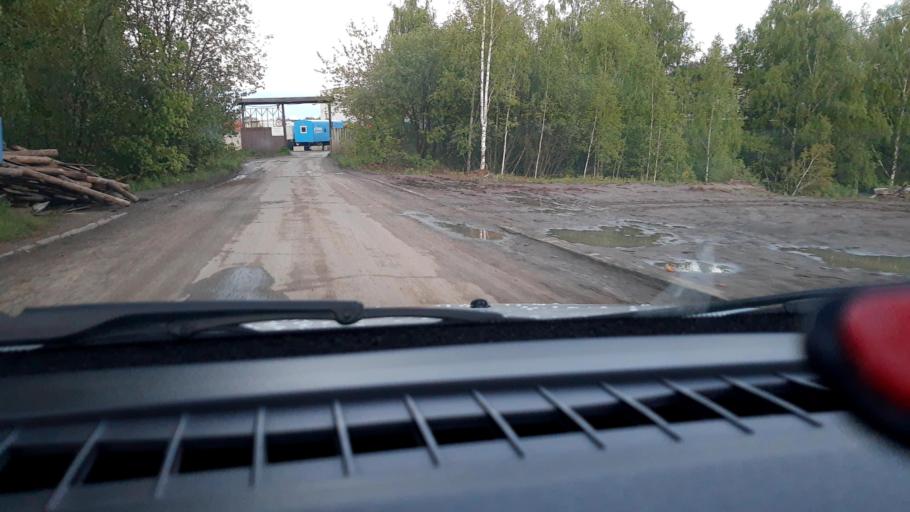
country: RU
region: Nizjnij Novgorod
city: Afonino
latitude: 56.2287
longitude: 44.0899
